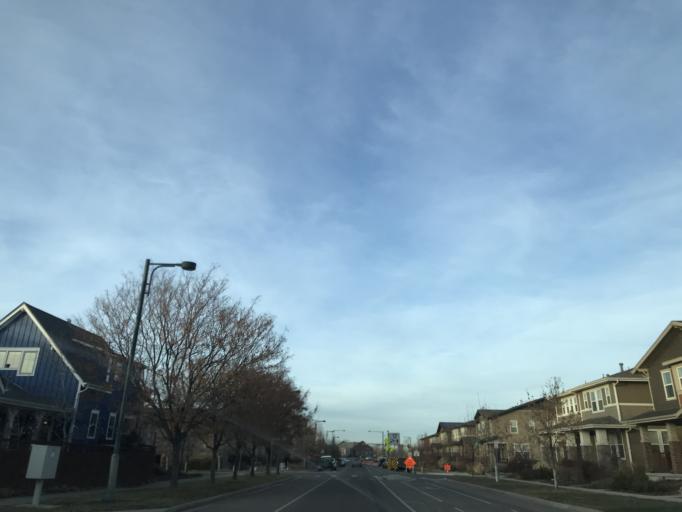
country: US
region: Colorado
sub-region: Adams County
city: Aurora
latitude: 39.7568
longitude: -104.8645
